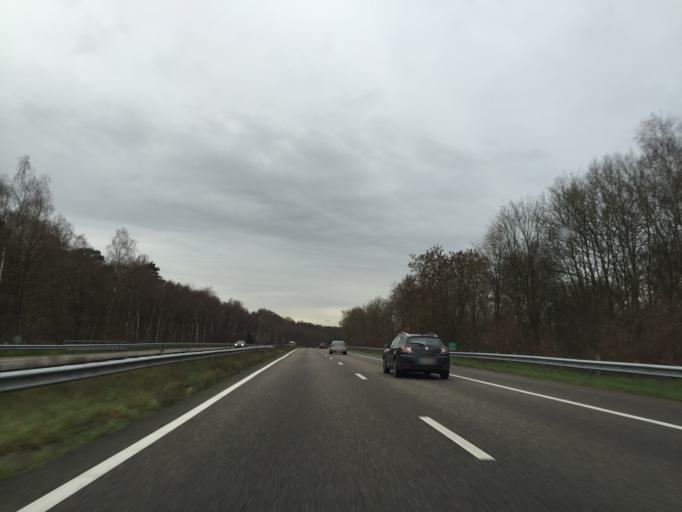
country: NL
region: North Brabant
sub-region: Gemeente Woensdrecht
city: Woensdrecht
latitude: 51.4607
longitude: 4.3120
